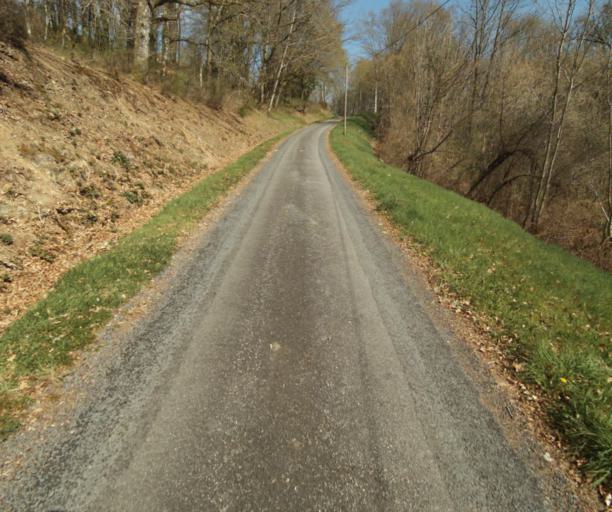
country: FR
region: Limousin
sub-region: Departement de la Correze
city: Naves
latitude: 45.3400
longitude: 1.7926
